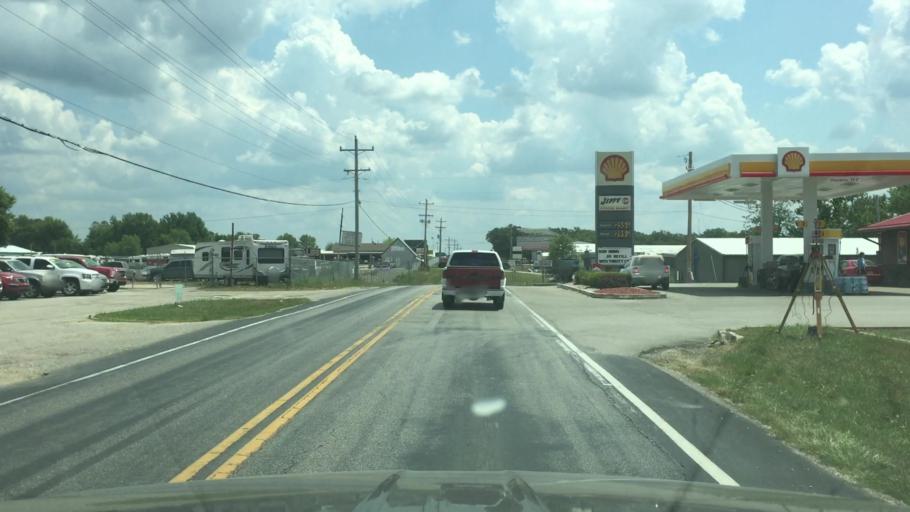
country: US
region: Missouri
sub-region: Camden County
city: Osage Beach
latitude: 38.1397
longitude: -92.5871
